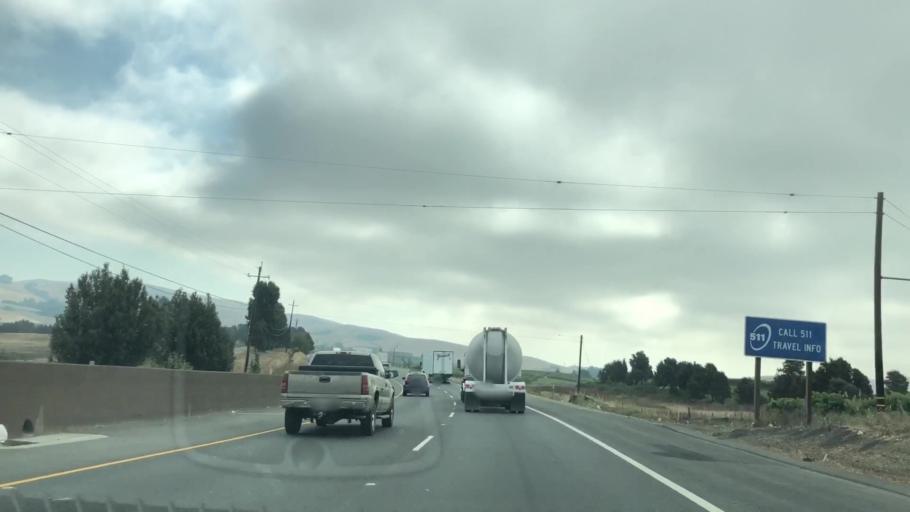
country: US
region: California
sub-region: Napa County
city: American Canyon
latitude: 38.2212
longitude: -122.2459
